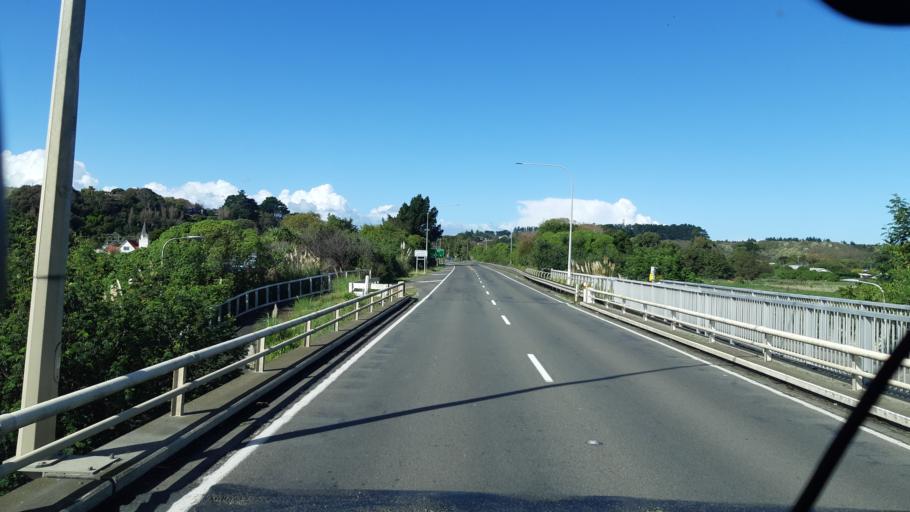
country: NZ
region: Manawatu-Wanganui
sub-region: Wanganui District
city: Wanganui
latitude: -39.9460
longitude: 175.0473
